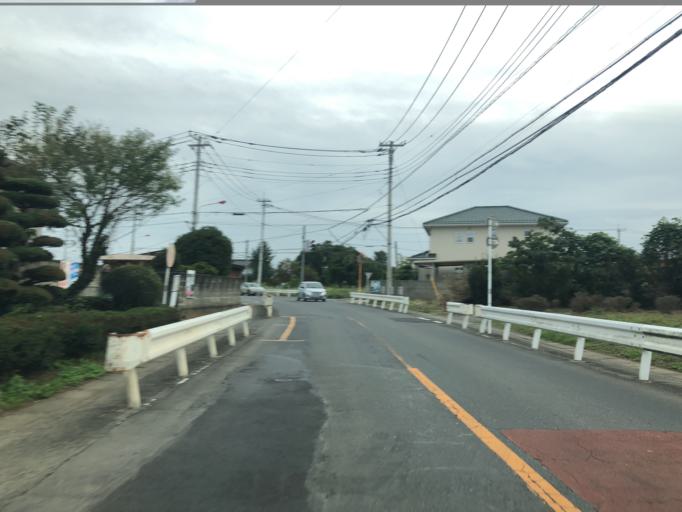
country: JP
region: Saitama
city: Fukiage-fujimi
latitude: 36.0495
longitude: 139.3902
